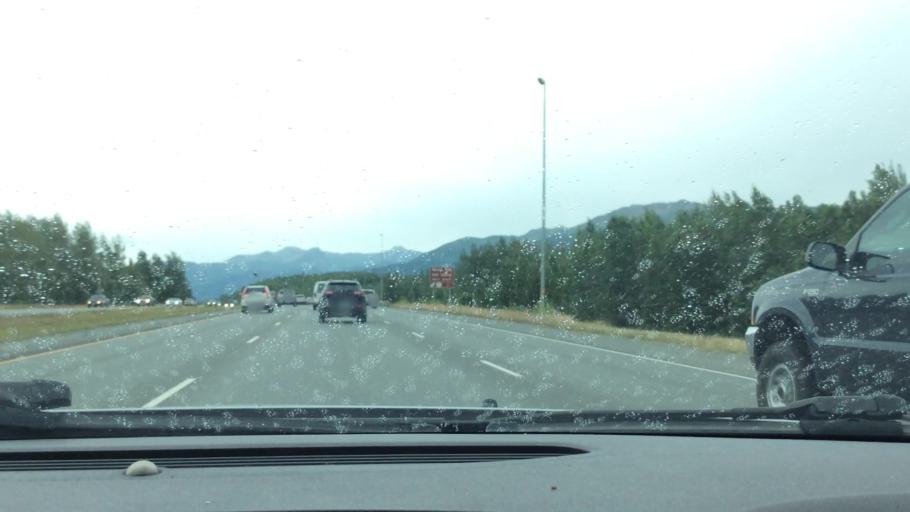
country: US
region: Alaska
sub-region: Anchorage Municipality
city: Elmendorf Air Force Base
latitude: 61.2365
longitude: -149.6985
